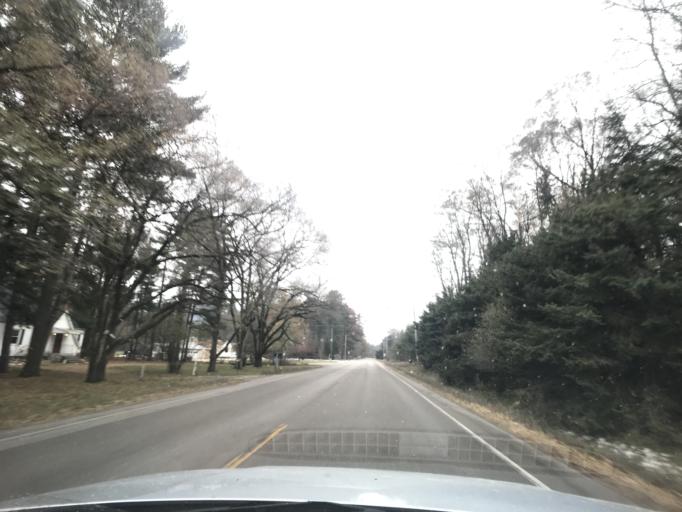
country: US
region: Wisconsin
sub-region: Marinette County
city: Marinette
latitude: 45.0679
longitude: -87.6193
